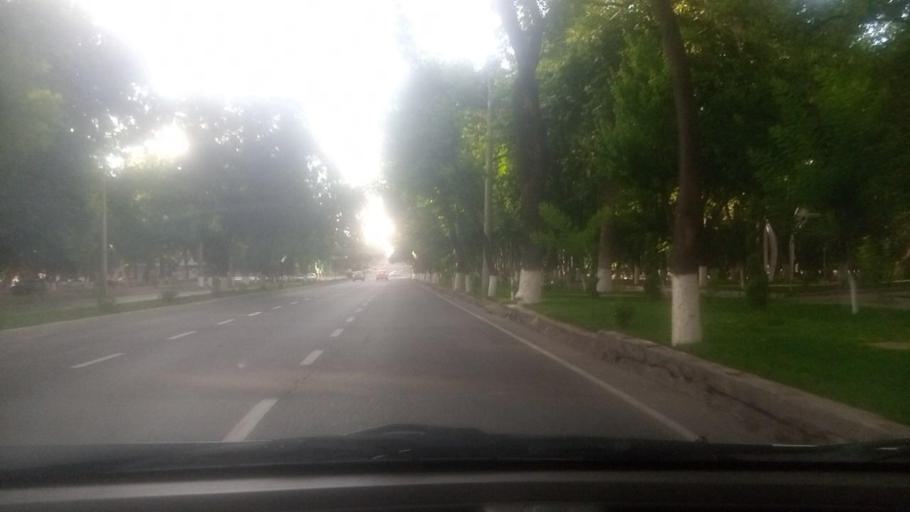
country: UZ
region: Toshkent
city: Salor
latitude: 41.3397
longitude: 69.3369
